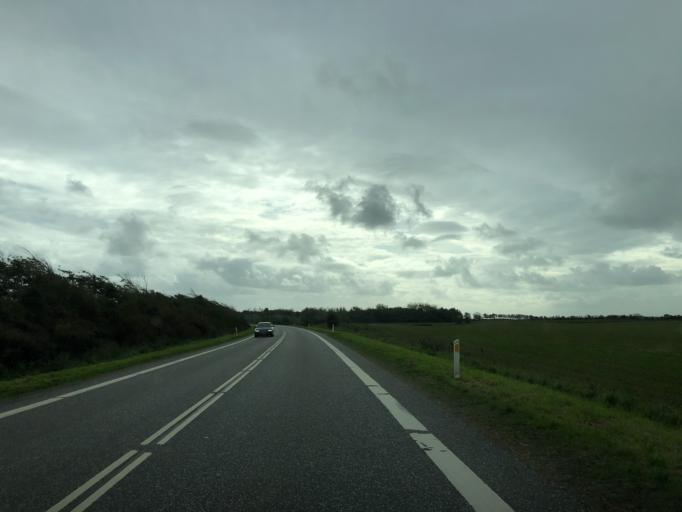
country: DK
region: North Denmark
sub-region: Thisted Kommune
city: Hurup
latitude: 56.7420
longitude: 8.4372
